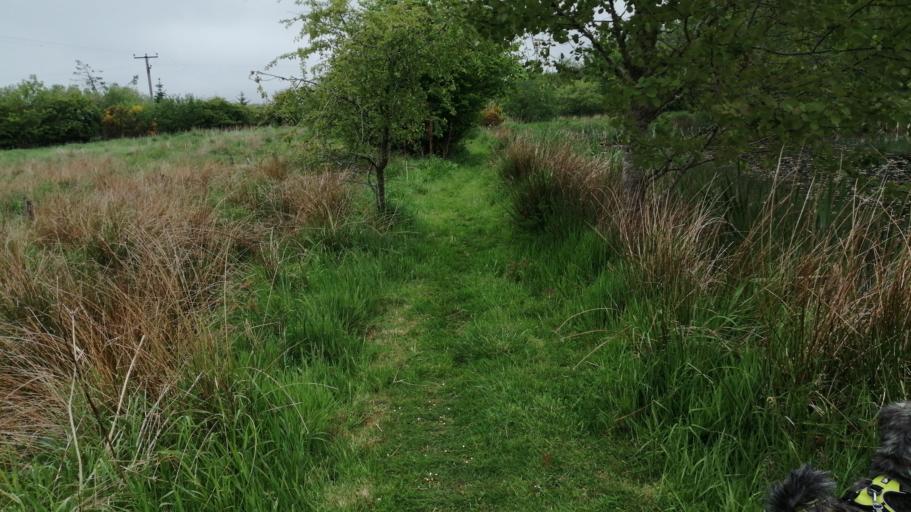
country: GB
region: Scotland
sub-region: Moray
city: Cullen
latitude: 57.5783
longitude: -2.7921
